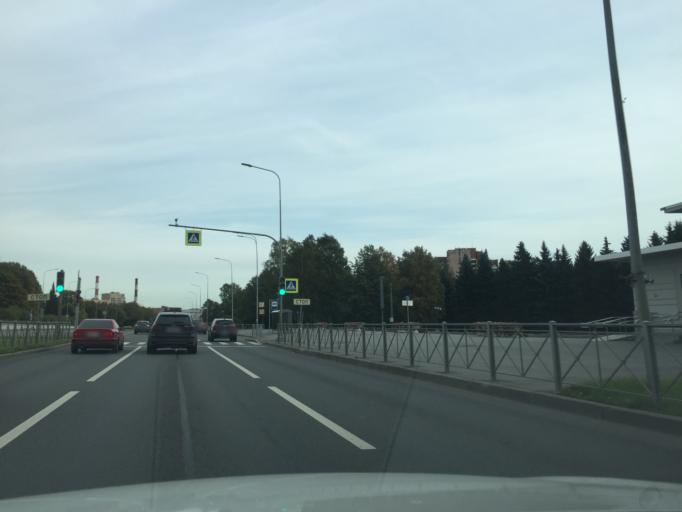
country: RU
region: Leningrad
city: Kalininskiy
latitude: 59.9941
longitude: 30.4187
